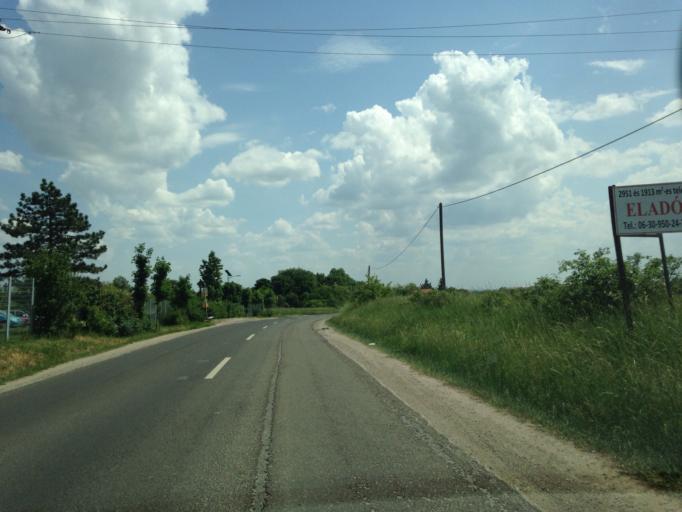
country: HU
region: Pest
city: Szentendre
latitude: 47.6888
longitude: 19.0535
